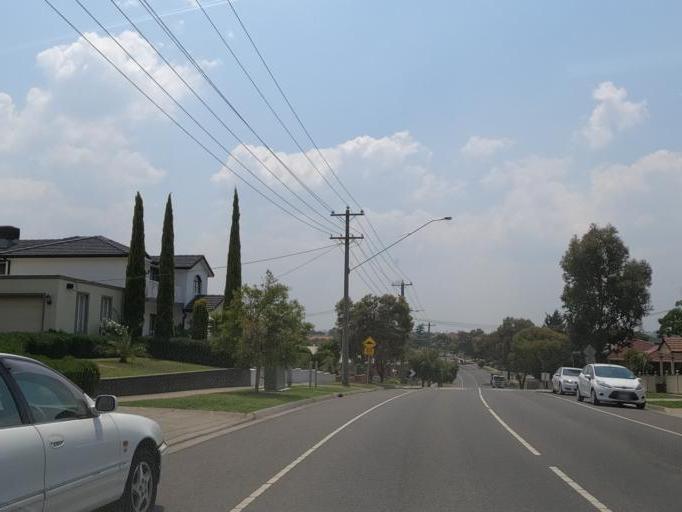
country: AU
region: Victoria
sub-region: Hume
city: Meadow Heights
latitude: -37.6497
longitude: 144.8966
